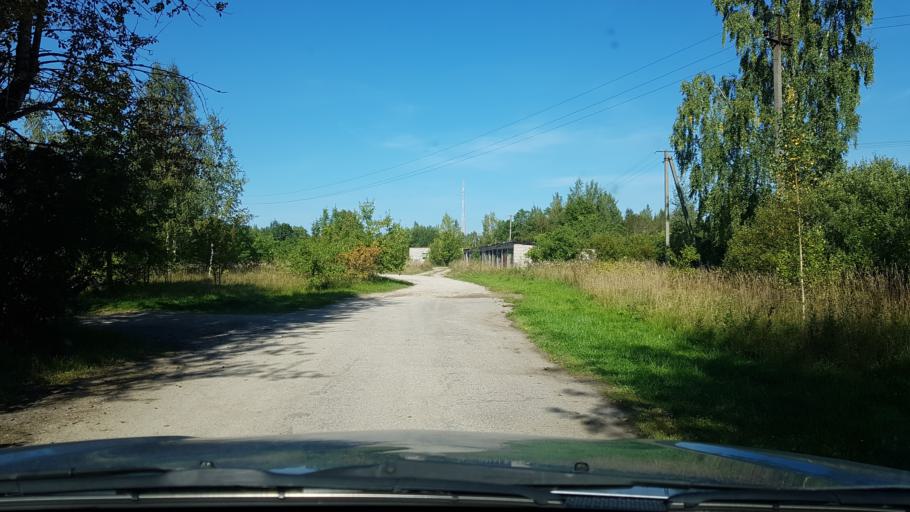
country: EE
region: Ida-Virumaa
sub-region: Sillamaee linn
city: Sillamae
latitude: 59.3229
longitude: 27.7790
